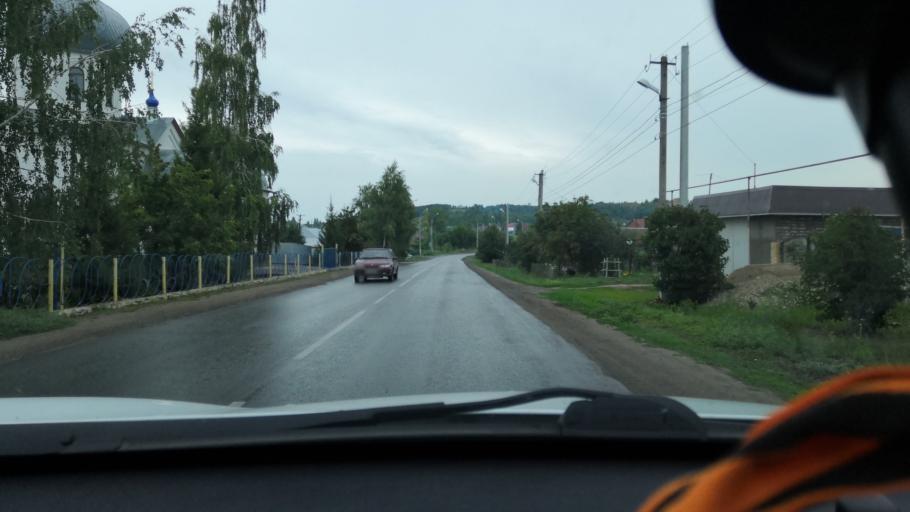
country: RU
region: Samara
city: Novosemeykino
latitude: 53.3765
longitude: 50.3482
